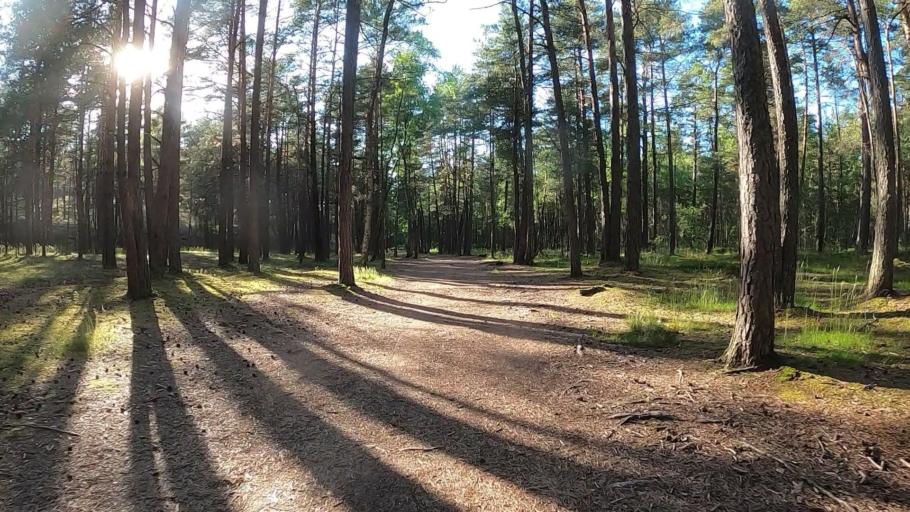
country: LV
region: Carnikava
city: Carnikava
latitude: 57.1374
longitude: 24.2455
